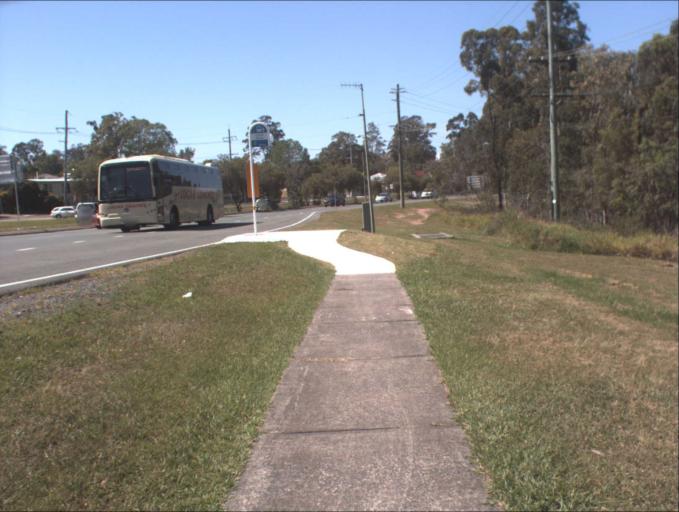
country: AU
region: Queensland
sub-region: Logan
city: Waterford West
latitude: -27.6696
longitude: 153.1220
